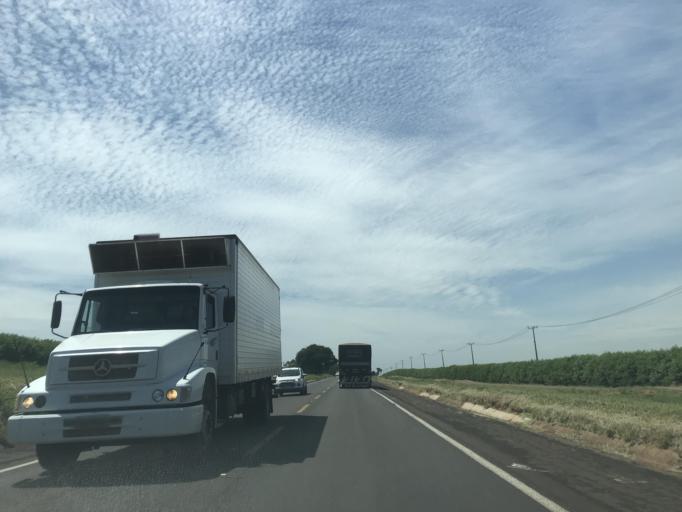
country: BR
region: Parana
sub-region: Paranavai
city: Nova Aurora
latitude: -22.9681
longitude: -52.6319
